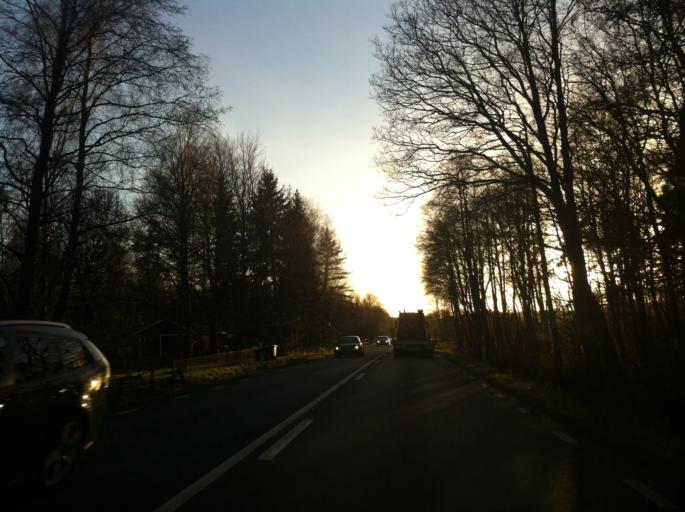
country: SE
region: Skane
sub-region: Hassleholms Kommun
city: Hassleholm
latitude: 56.1778
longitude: 13.8421
